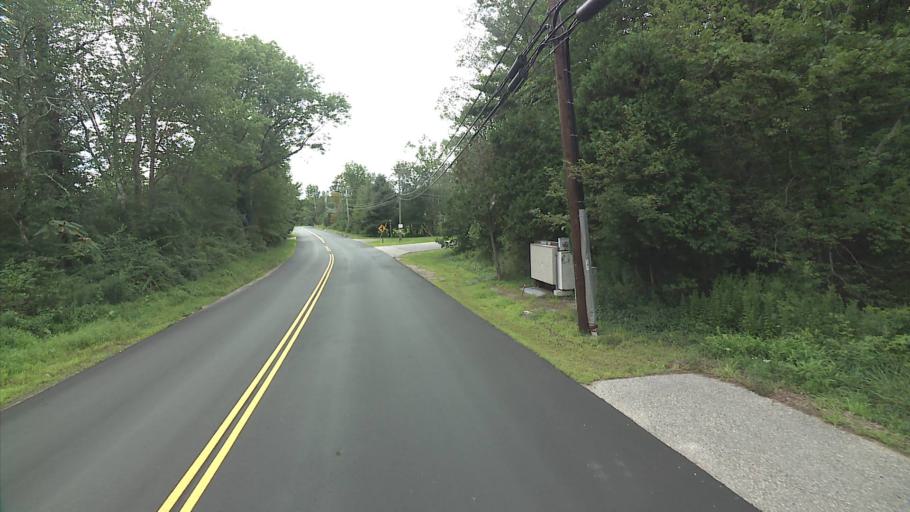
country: US
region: Connecticut
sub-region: Windham County
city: South Woodstock
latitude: 41.9499
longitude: -72.0588
